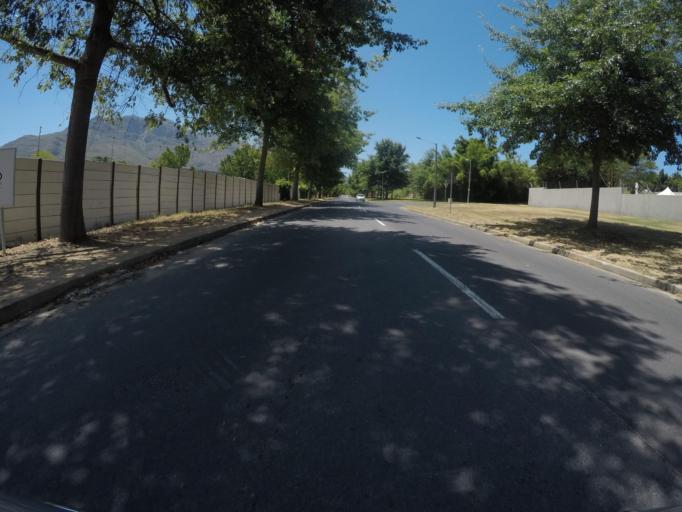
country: ZA
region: Western Cape
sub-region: Cape Winelands District Municipality
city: Stellenbosch
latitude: -33.9625
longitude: 18.8569
